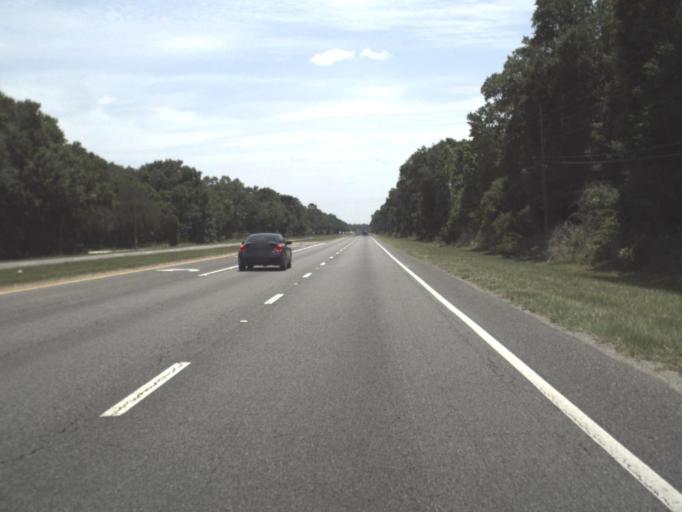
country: US
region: Florida
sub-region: Dixie County
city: Cross City
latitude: 29.6025
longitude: -83.0143
